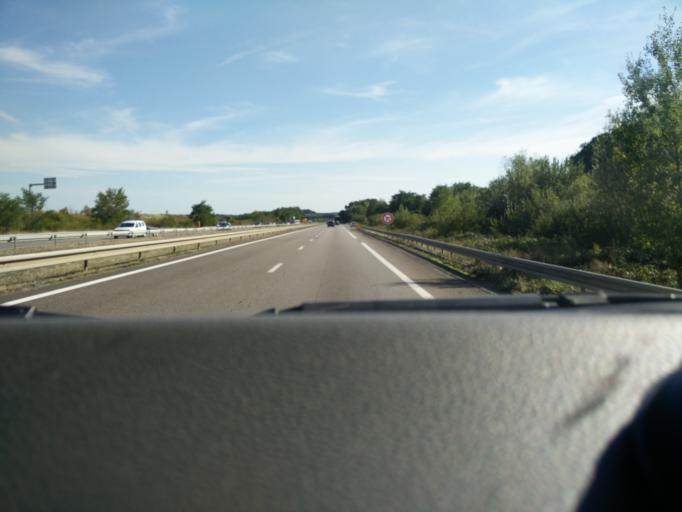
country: FR
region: Lorraine
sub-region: Departement de la Moselle
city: Augny
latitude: 49.0359
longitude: 6.1129
